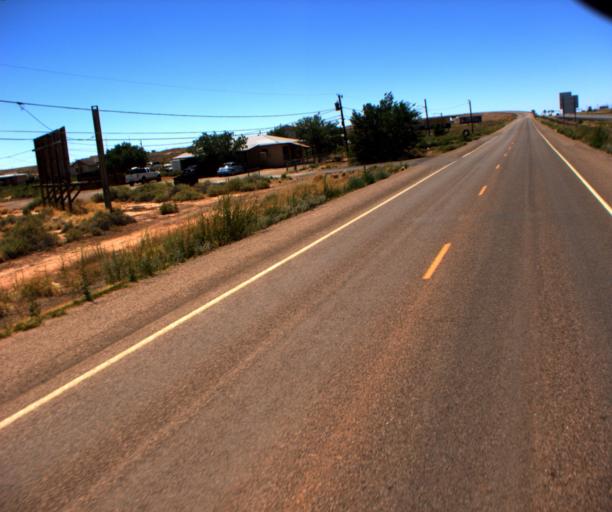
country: US
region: Arizona
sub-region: Coconino County
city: LeChee
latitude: 35.0387
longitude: -110.7358
